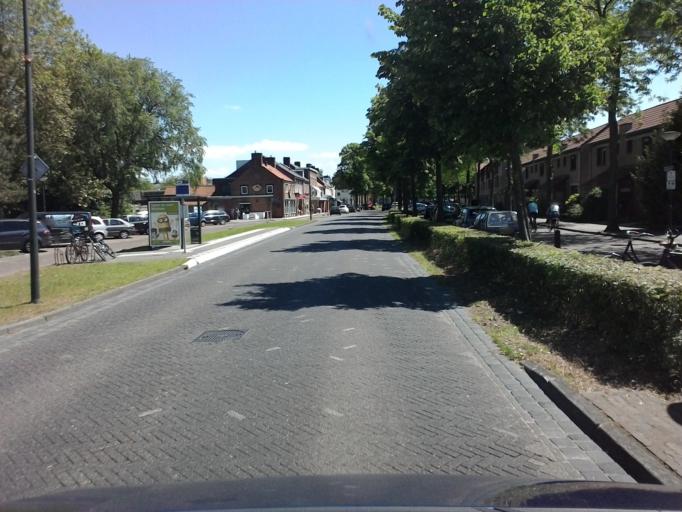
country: NL
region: North Brabant
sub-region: Gemeente Schijndel
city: Schijndel
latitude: 51.6159
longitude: 5.4408
